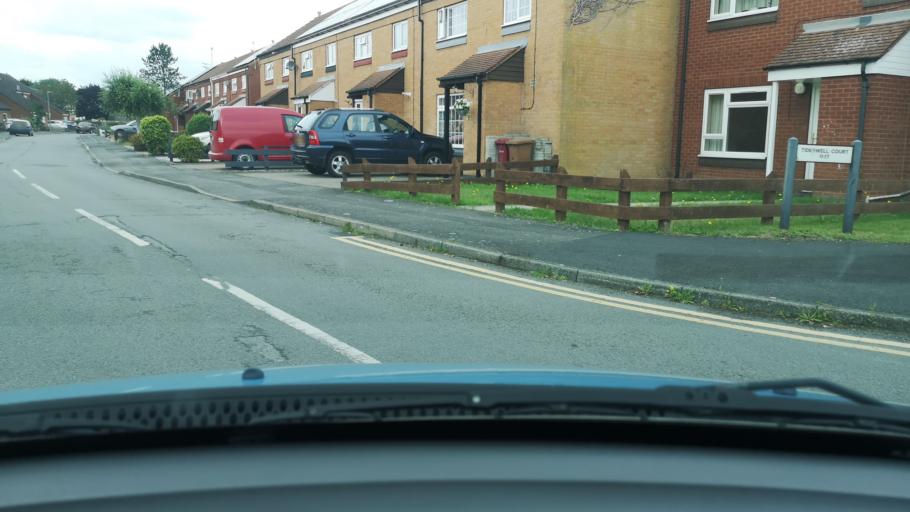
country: GB
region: England
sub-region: North Lincolnshire
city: Scunthorpe
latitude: 53.5874
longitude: -0.6887
